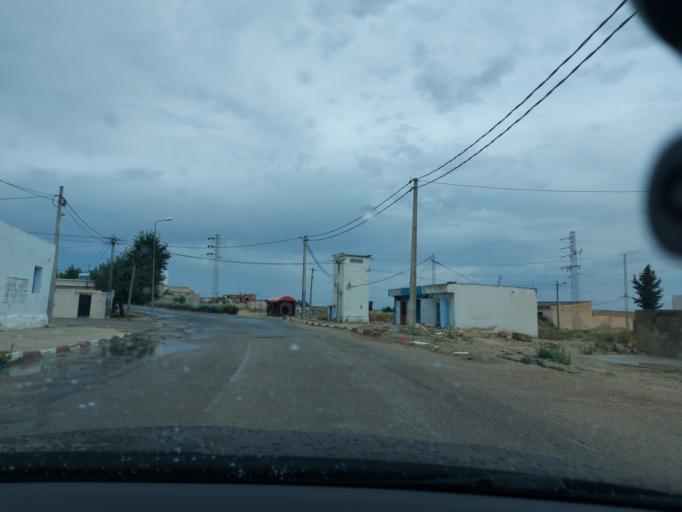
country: TN
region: Silyanah
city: Maktar
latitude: 35.8546
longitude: 9.2118
